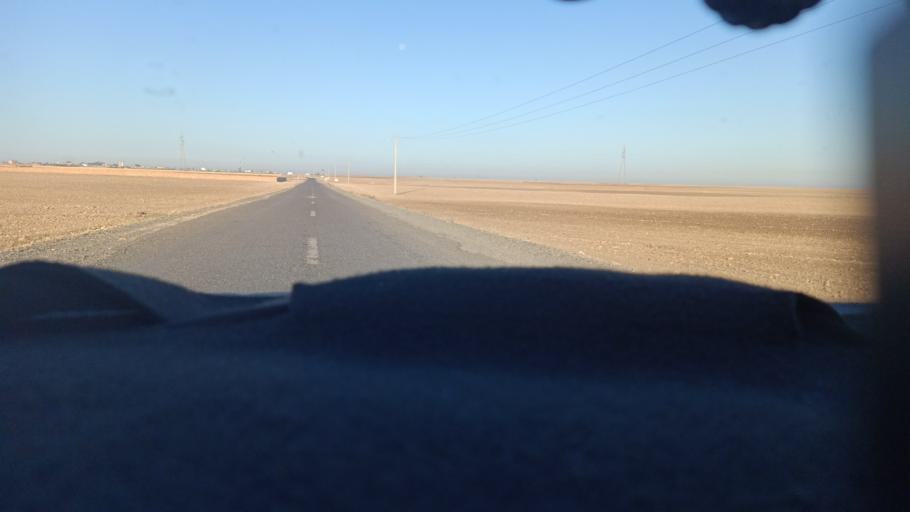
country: MA
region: Doukkala-Abda
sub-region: Safi
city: Youssoufia
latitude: 32.3708
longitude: -8.6566
